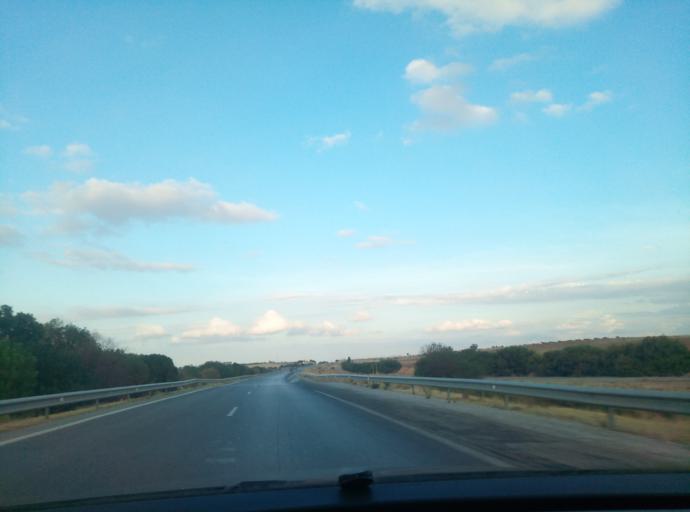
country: TN
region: Manouba
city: El Battan
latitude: 36.6598
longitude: 9.8093
